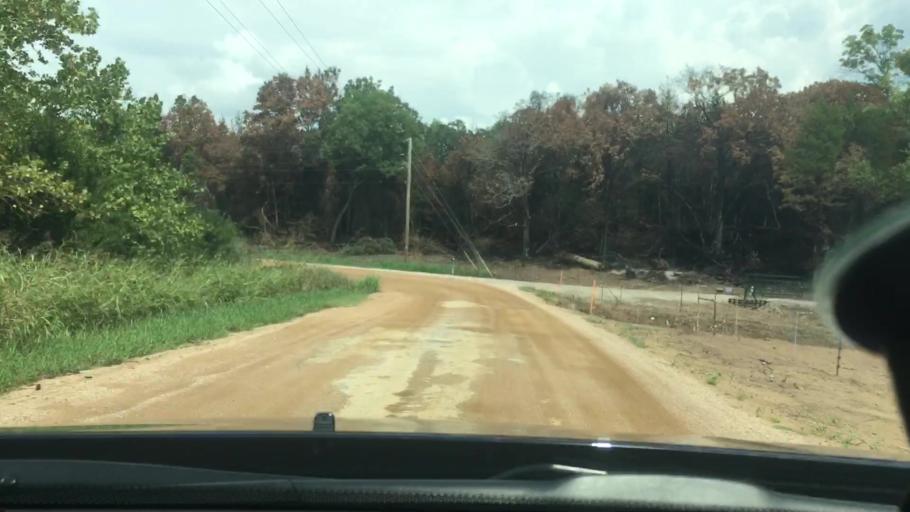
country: US
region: Oklahoma
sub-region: Carter County
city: Dickson
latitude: 34.2401
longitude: -96.9157
